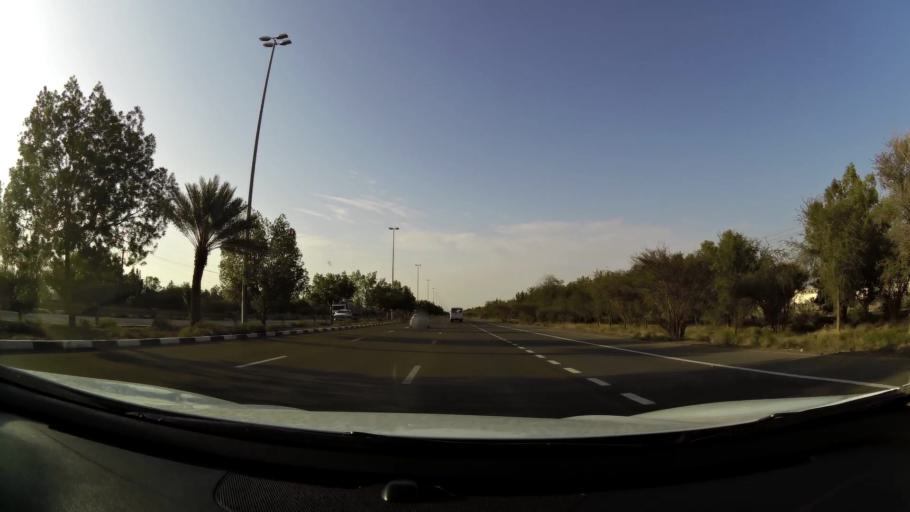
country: AE
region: Abu Dhabi
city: Al Ain
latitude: 24.1333
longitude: 55.8185
